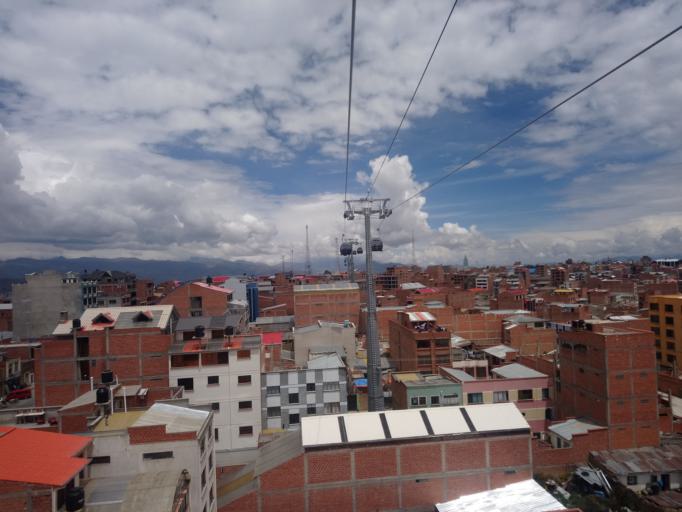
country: BO
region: La Paz
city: La Paz
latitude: -16.4961
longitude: -68.1703
